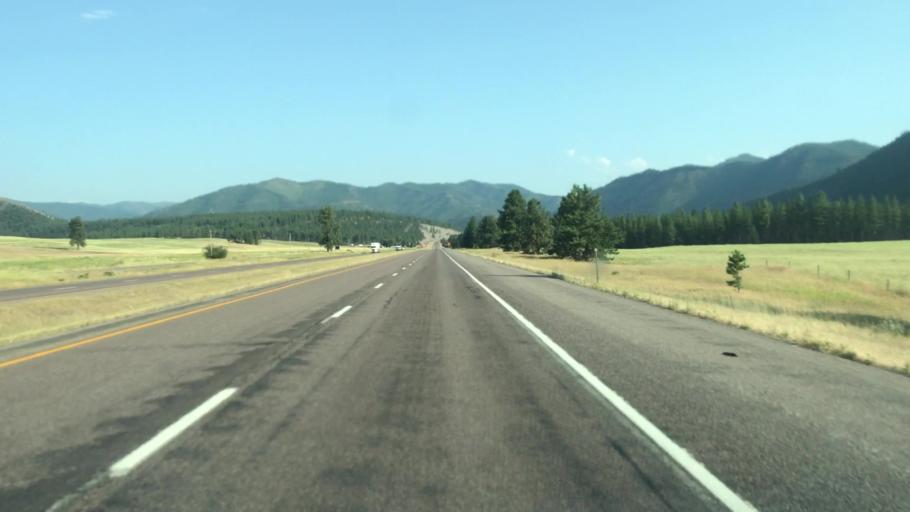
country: US
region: Montana
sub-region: Mineral County
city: Superior
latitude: 47.0412
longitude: -114.7497
